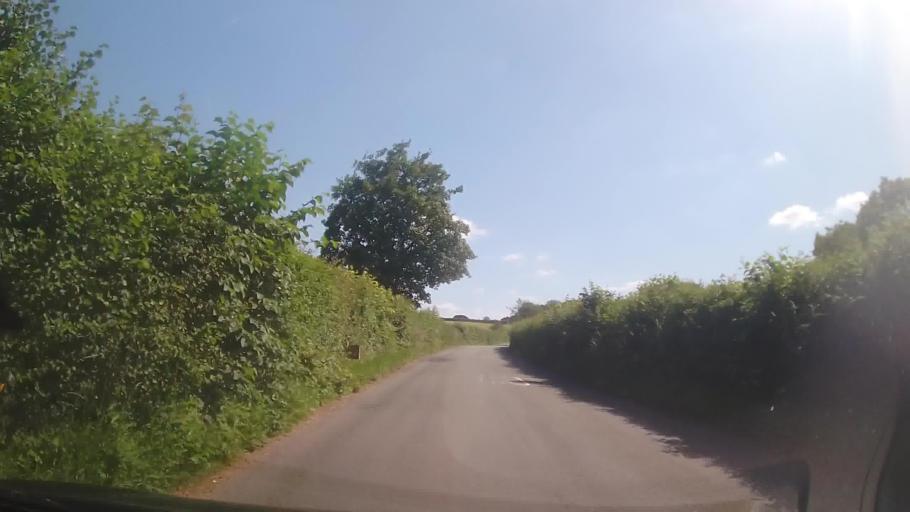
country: GB
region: England
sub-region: Herefordshire
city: Withington
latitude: 52.0748
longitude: -2.6360
